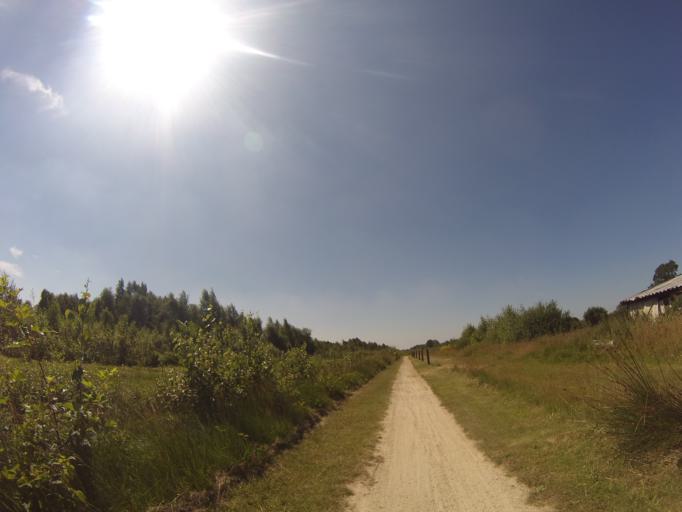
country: DE
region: Lower Saxony
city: Twist
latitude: 52.6669
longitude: 7.0156
